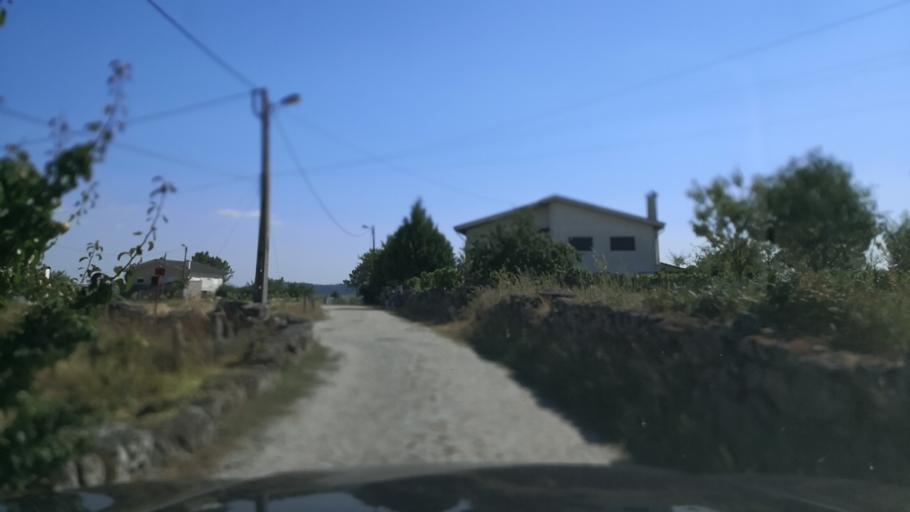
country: PT
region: Vila Real
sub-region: Murca
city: Murca
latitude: 41.3240
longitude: -7.4890
